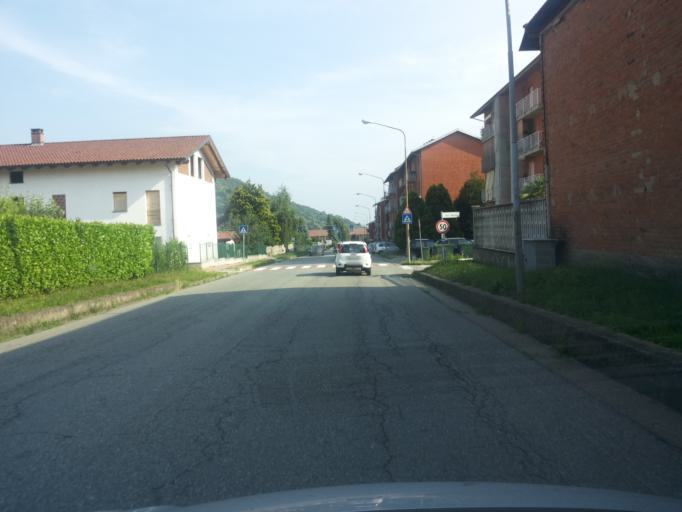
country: IT
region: Piedmont
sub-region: Provincia di Biella
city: Andorno Cacciorna
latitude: 45.6110
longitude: 8.0525
